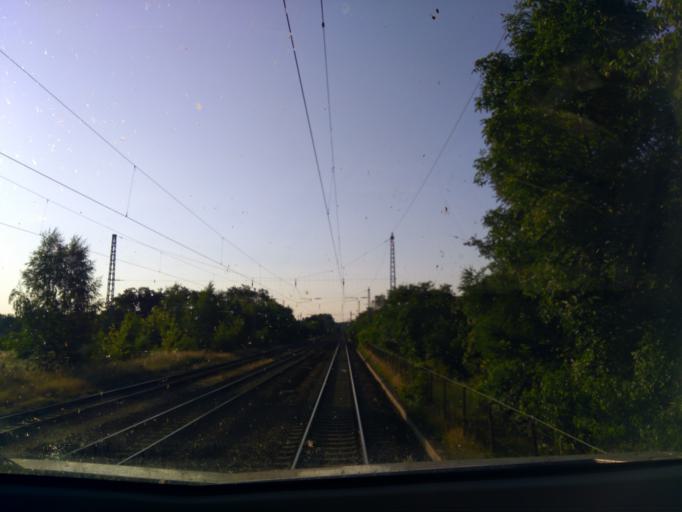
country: DE
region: Brandenburg
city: Vetschau
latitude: 51.7882
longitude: 14.0858
